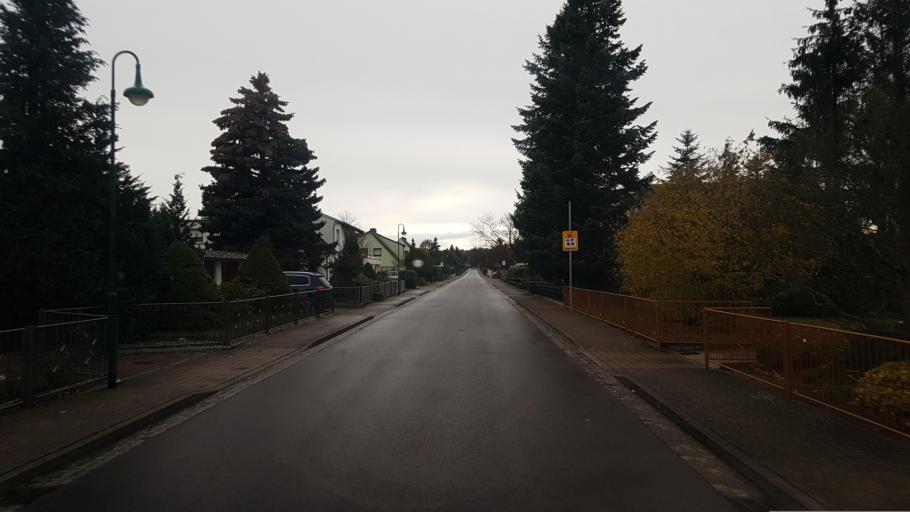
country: DE
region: Saxony-Anhalt
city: Abtsdorf
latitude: 51.8777
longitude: 12.7396
